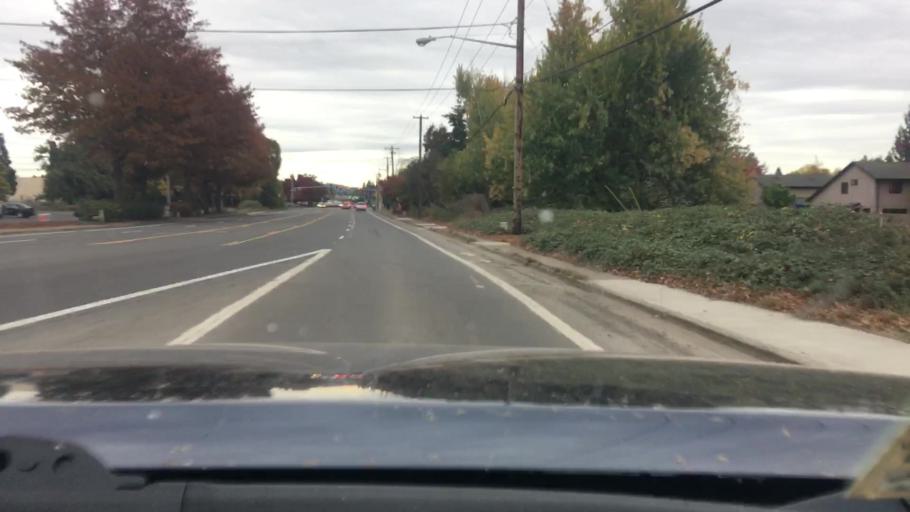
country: US
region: Oregon
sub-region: Lane County
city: Coburg
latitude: 44.0955
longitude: -123.0679
